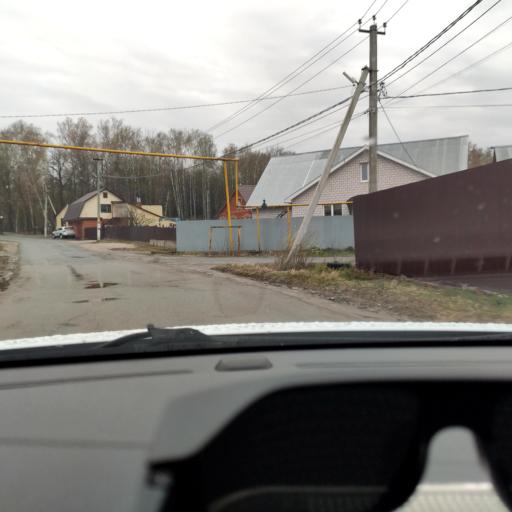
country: RU
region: Tatarstan
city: Vysokaya Gora
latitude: 55.9281
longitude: 49.3039
